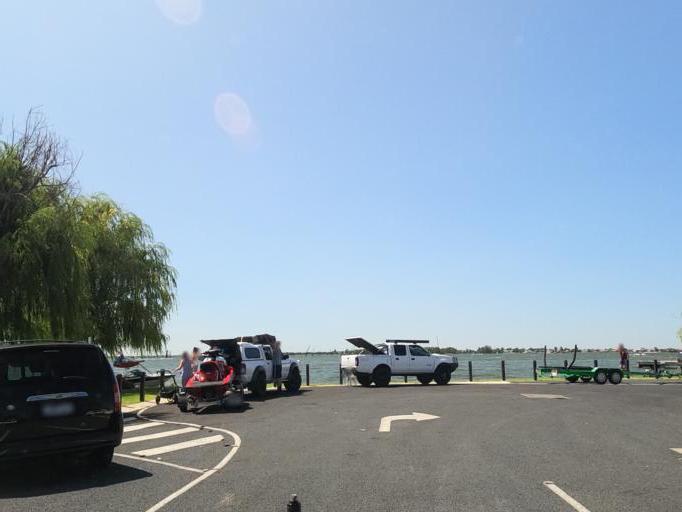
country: AU
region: New South Wales
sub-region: Corowa Shire
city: Mulwala
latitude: -35.9883
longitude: 146.0071
